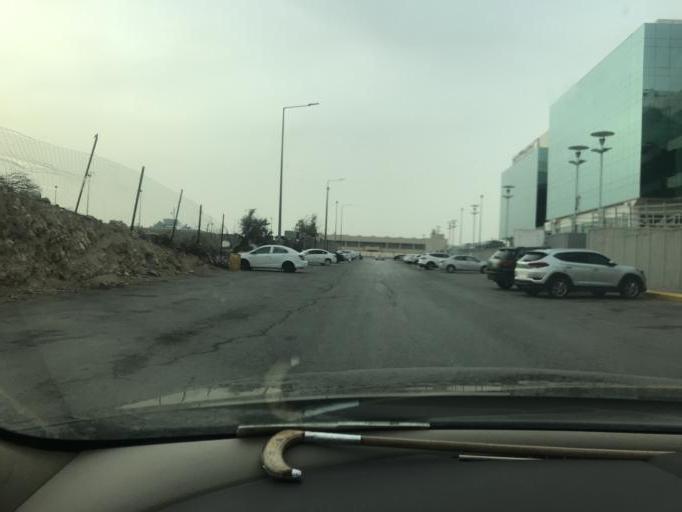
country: SA
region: Ar Riyad
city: Riyadh
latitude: 24.7204
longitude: 46.7747
